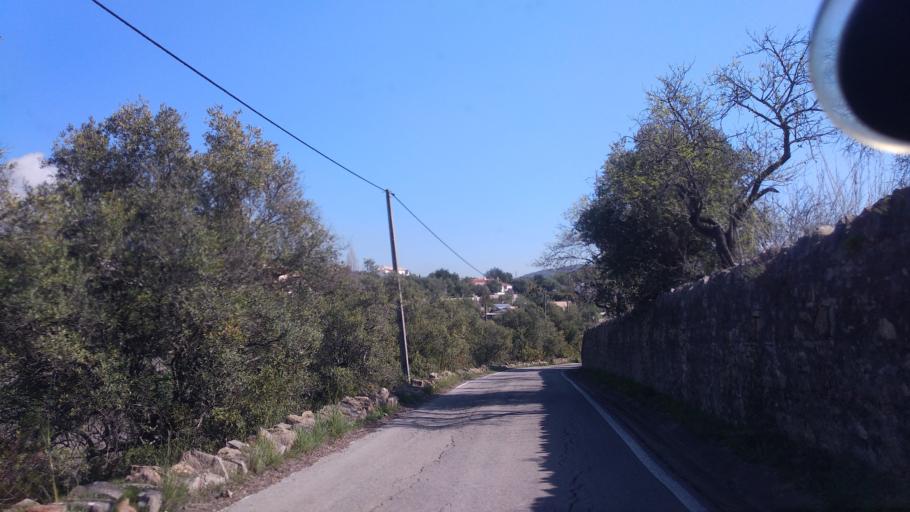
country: PT
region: Faro
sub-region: Faro
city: Santa Barbara de Nexe
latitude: 37.1118
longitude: -7.9277
